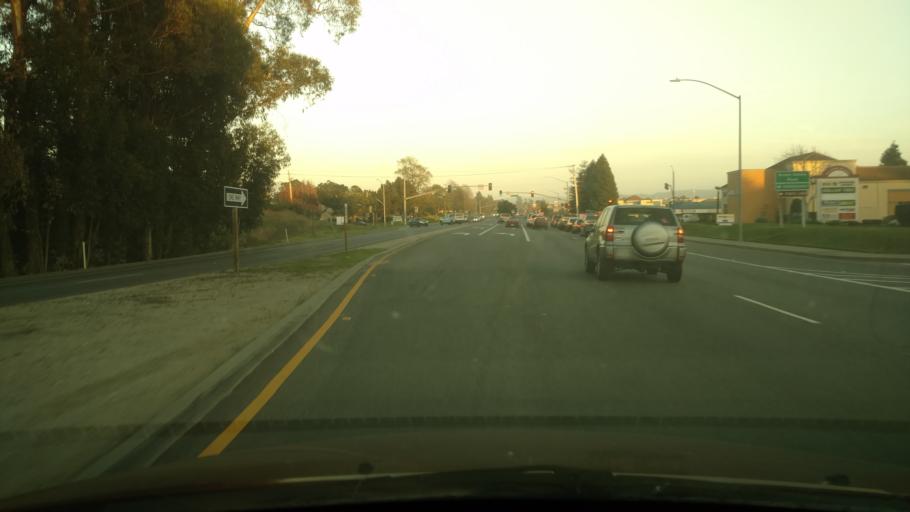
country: US
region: California
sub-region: Santa Cruz County
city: Freedom
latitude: 36.9189
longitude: -121.7856
